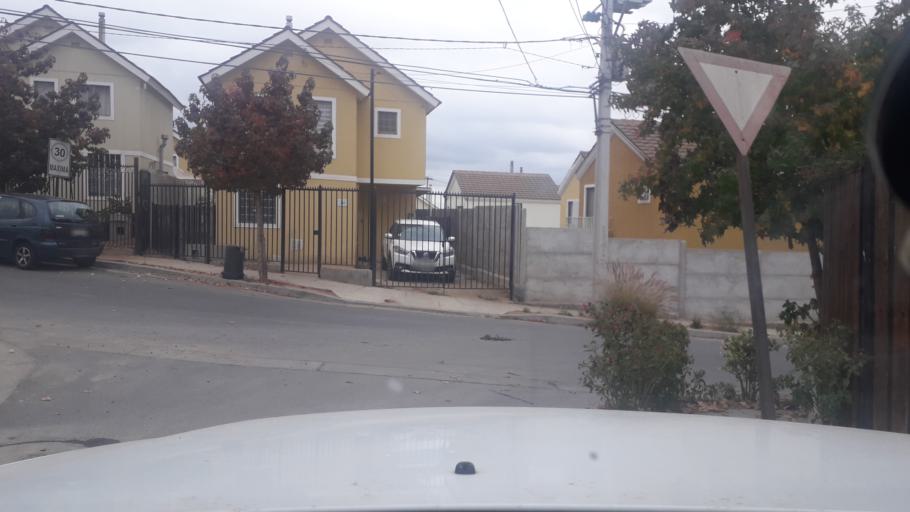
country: CL
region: Valparaiso
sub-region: Provincia de Marga Marga
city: Villa Alemana
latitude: -33.0513
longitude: -71.3342
